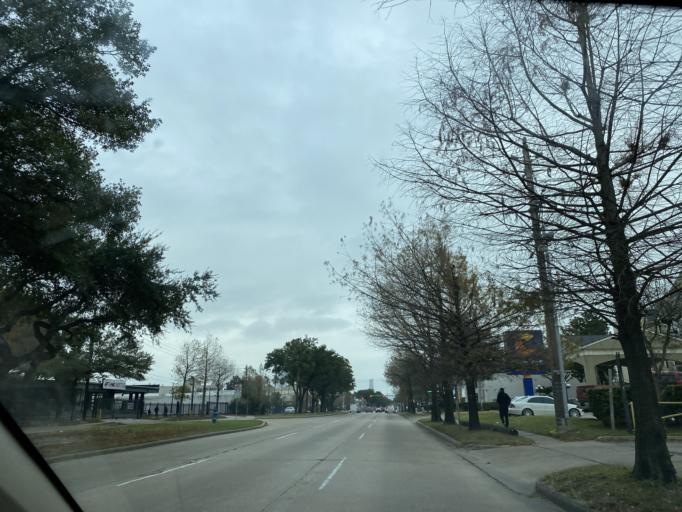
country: US
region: Texas
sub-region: Harris County
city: Piney Point Village
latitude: 29.7317
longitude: -95.4919
